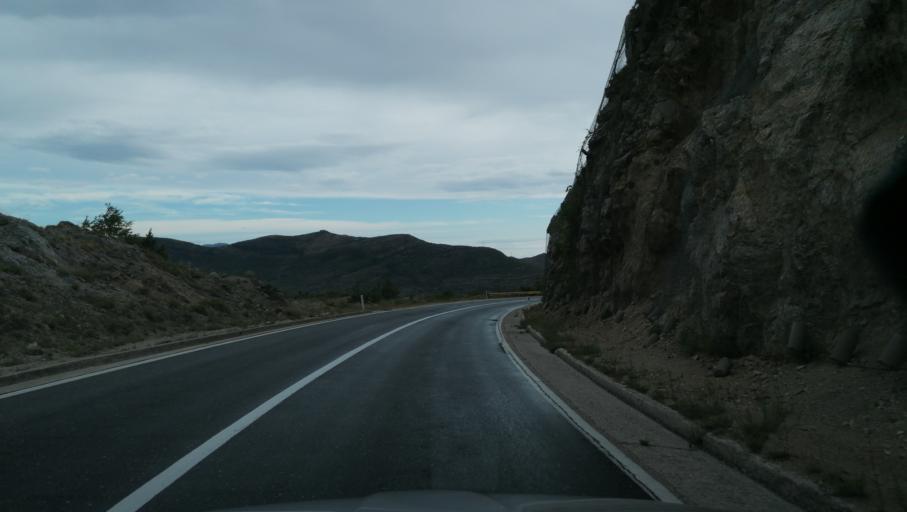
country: BA
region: Republika Srpska
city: Trebinje
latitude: 42.7273
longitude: 18.3942
